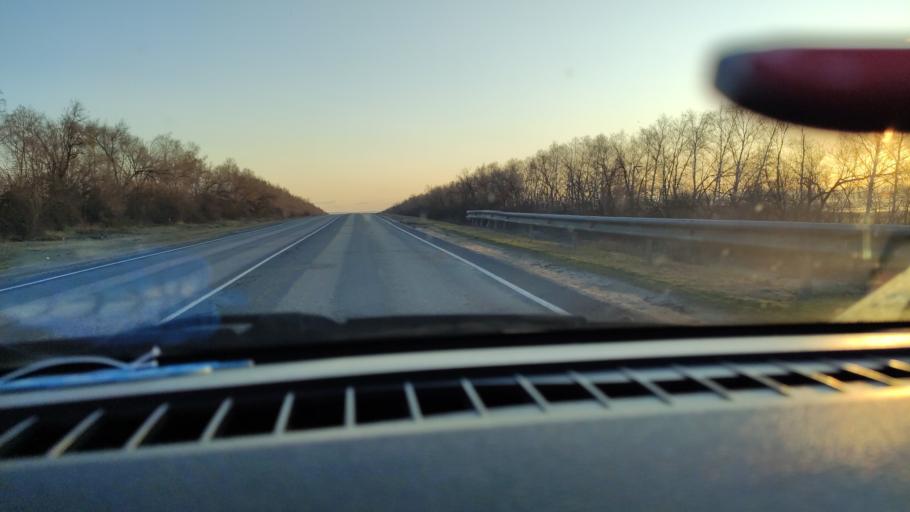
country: RU
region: Saratov
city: Sinodskoye
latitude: 51.9425
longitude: 46.5985
